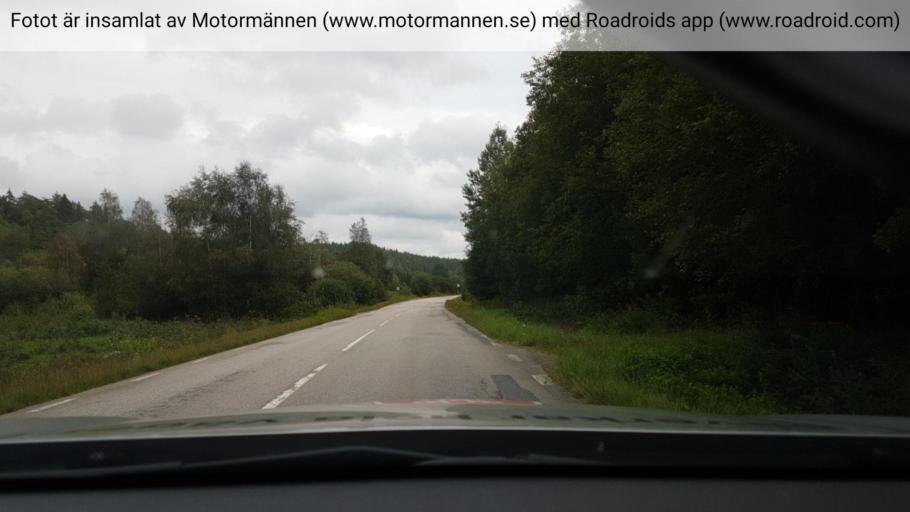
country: SE
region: Vaestra Goetaland
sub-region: Lysekils Kommun
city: Brastad
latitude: 58.5538
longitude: 11.4974
